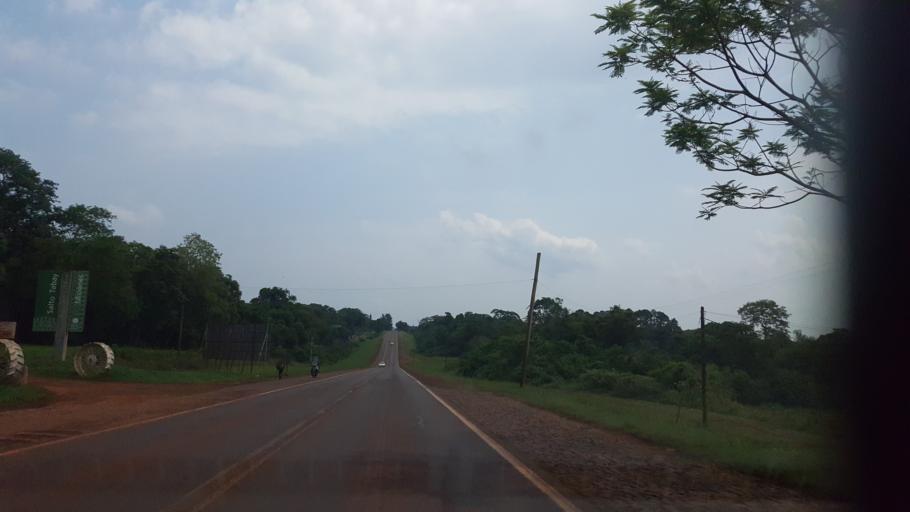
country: AR
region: Misiones
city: Jardin America
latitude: -27.0505
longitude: -55.2481
